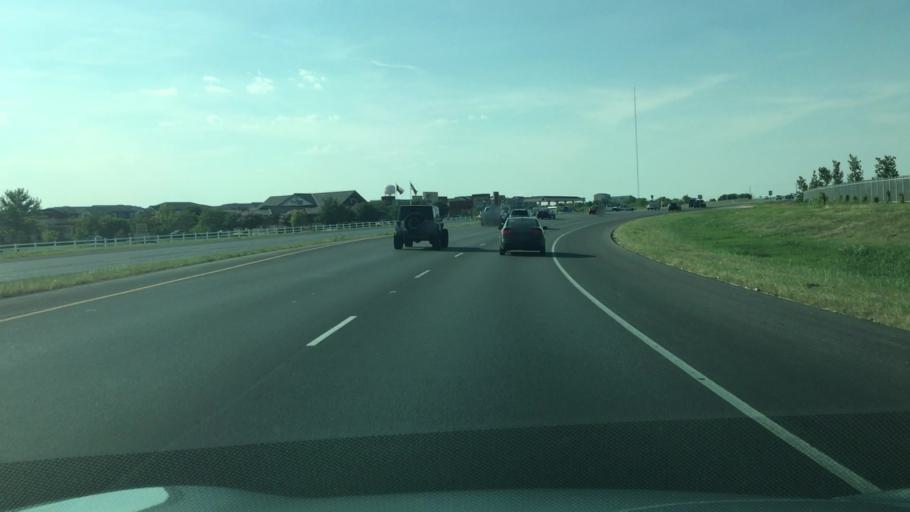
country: US
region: Texas
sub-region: Hays County
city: Kyle
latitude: 30.0193
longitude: -97.8716
